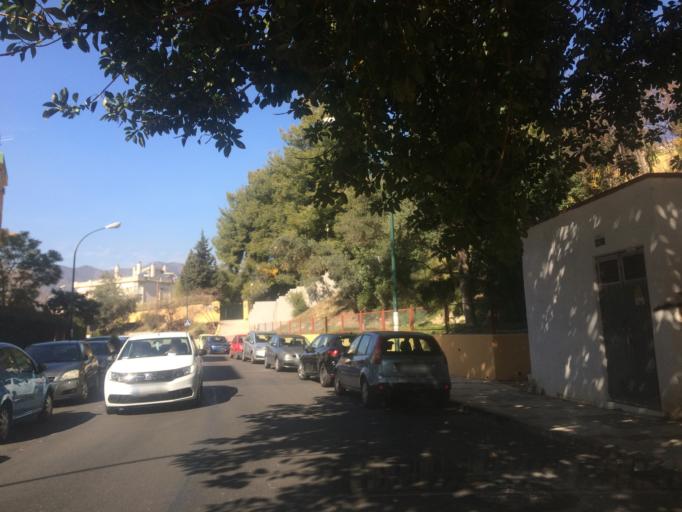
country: ES
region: Andalusia
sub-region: Provincia de Malaga
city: Malaga
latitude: 36.7505
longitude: -4.4154
